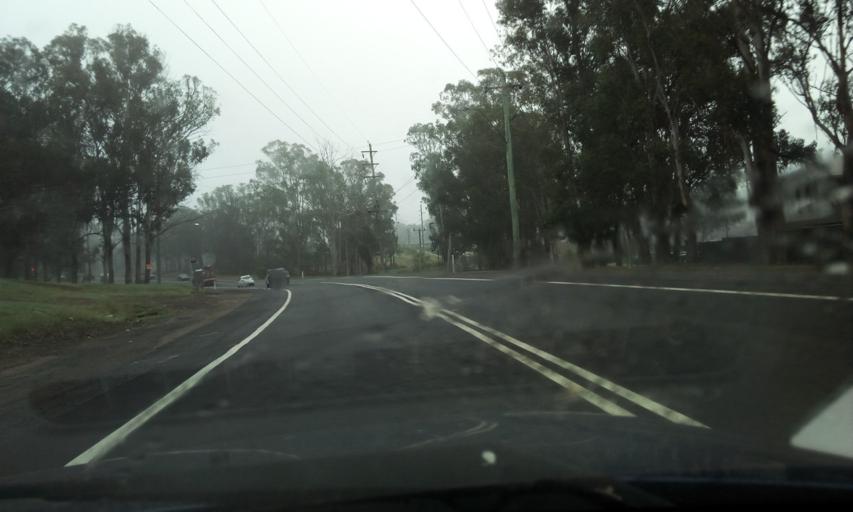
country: AU
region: New South Wales
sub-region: Penrith Municipality
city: Werrington Downs
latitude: -33.7174
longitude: 150.7262
